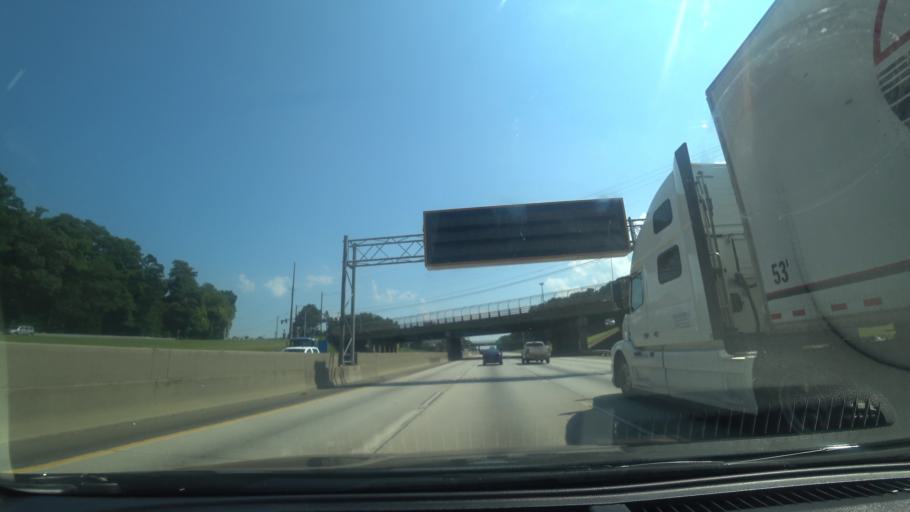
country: US
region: Georgia
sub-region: DeKalb County
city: Belvedere Park
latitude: 33.7536
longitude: -84.2322
